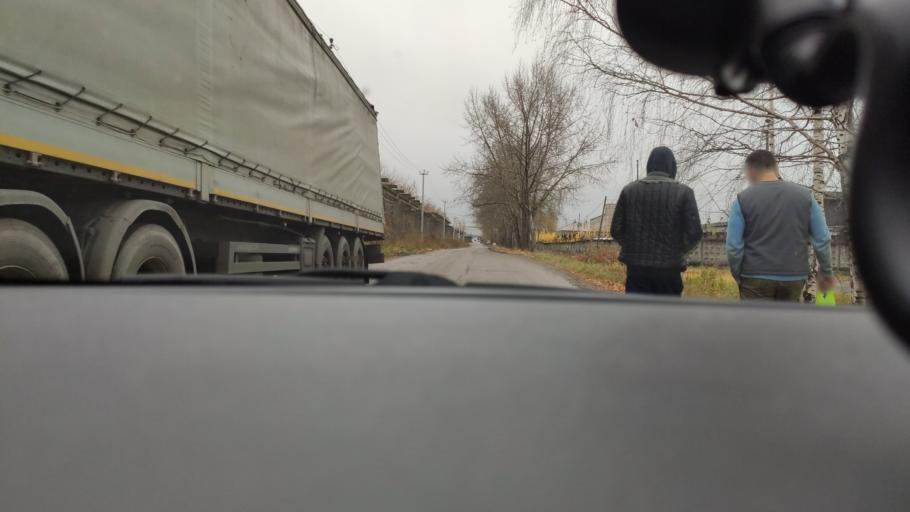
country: RU
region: Perm
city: Gamovo
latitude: 57.9159
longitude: 56.1726
